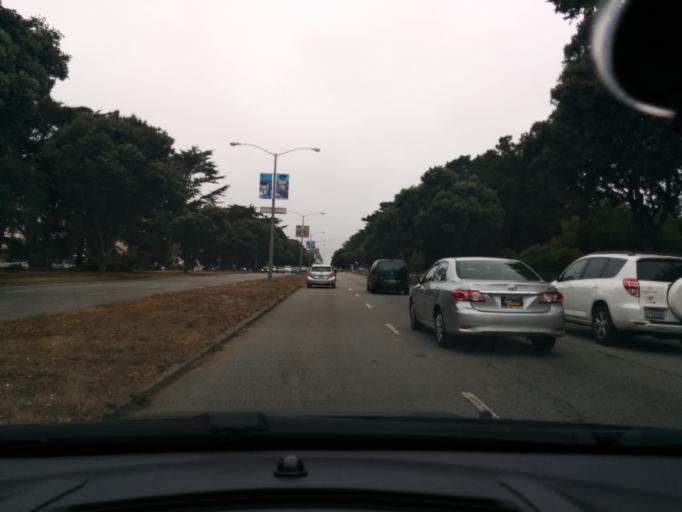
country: US
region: California
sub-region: San Mateo County
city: Daly City
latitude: 37.7461
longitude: -122.4947
